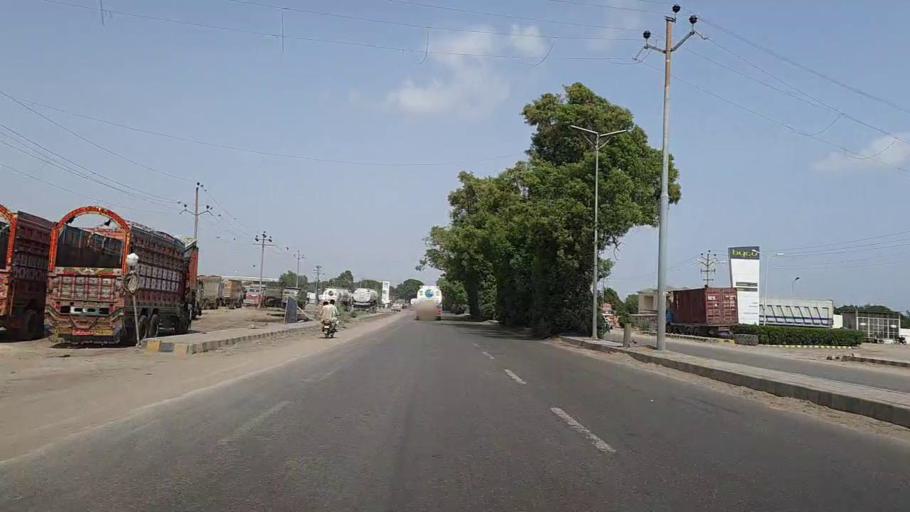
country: PK
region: Sindh
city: Malir Cantonment
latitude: 24.8626
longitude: 67.3200
